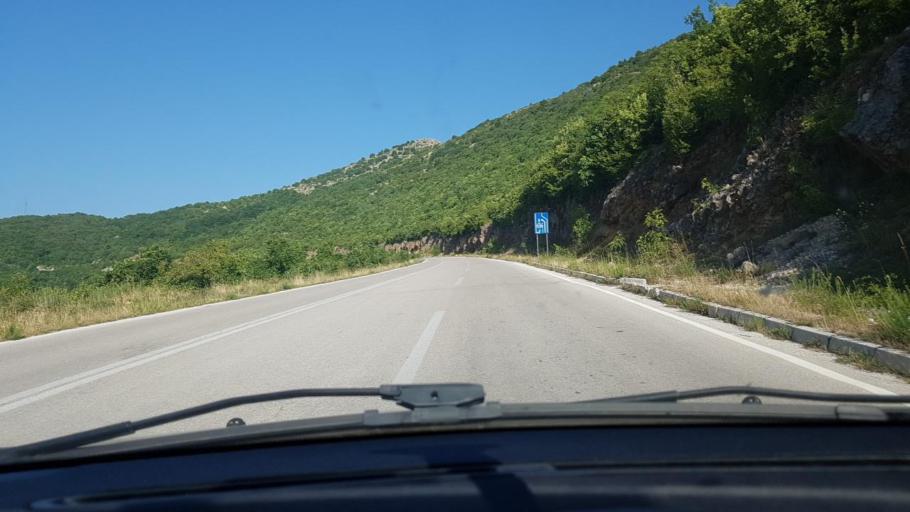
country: BA
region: Federation of Bosnia and Herzegovina
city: Rumboci
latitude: 43.8200
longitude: 17.4576
